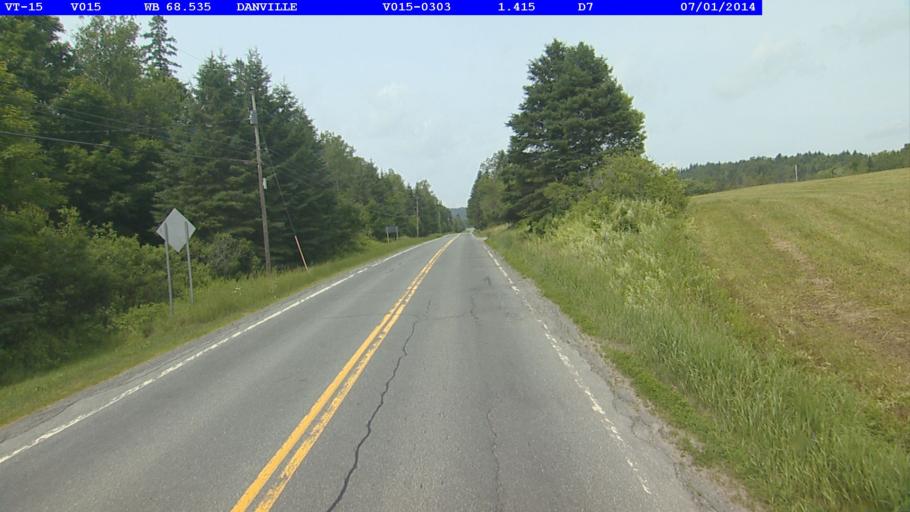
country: US
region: Vermont
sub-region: Caledonia County
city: Saint Johnsbury
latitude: 44.4111
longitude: -72.2026
